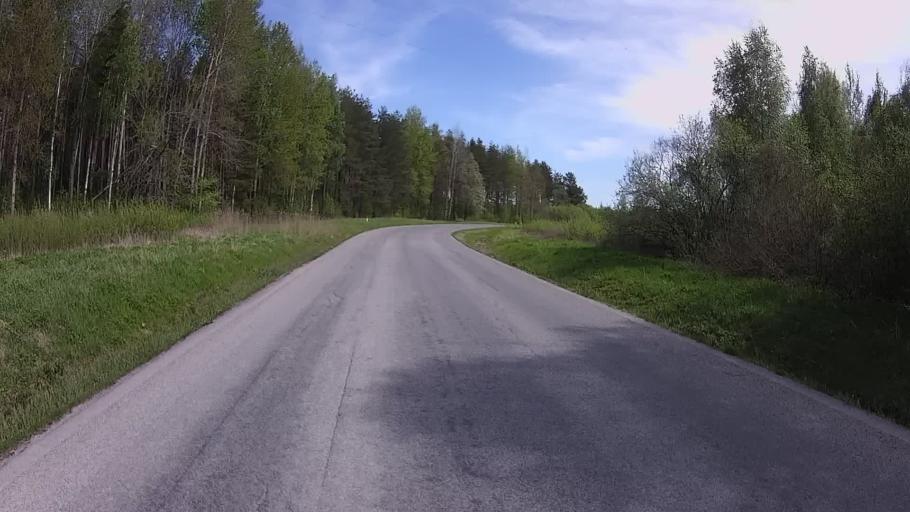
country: EE
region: Valgamaa
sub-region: Valga linn
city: Valga
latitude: 57.7773
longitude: 26.0696
